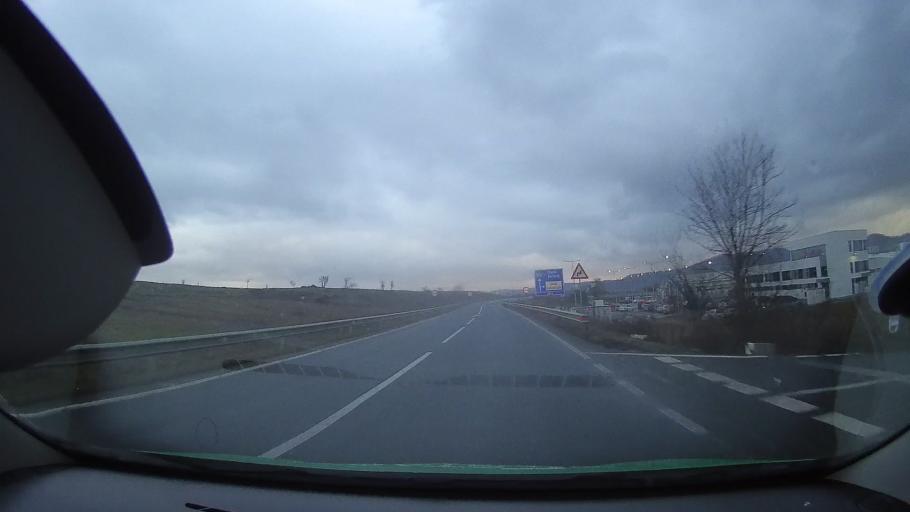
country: RO
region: Hunedoara
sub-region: Comuna Ribita
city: Ribita
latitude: 46.1639
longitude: 22.7544
